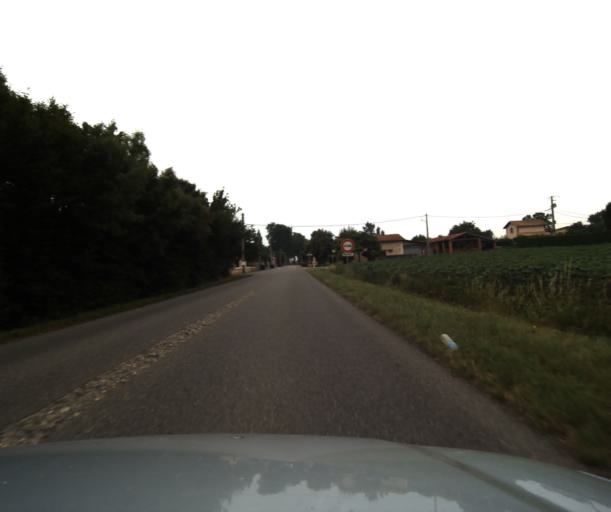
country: FR
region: Midi-Pyrenees
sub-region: Departement du Tarn-et-Garonne
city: Beaumont-de-Lomagne
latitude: 43.8526
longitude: 0.9428
